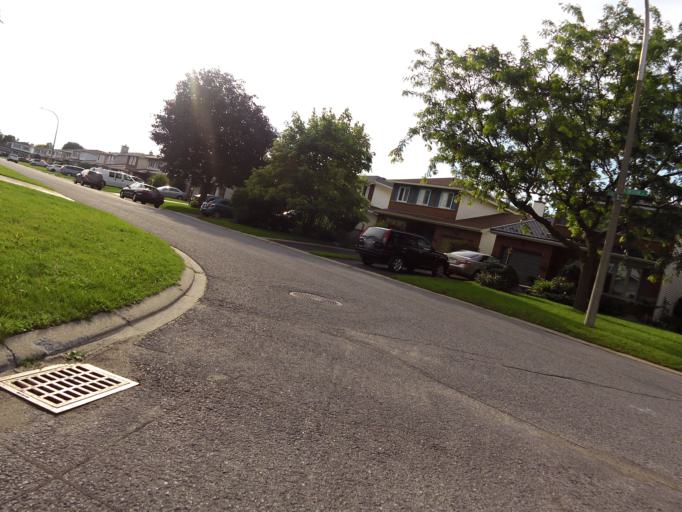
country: CA
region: Ontario
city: Ottawa
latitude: 45.3376
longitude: -75.7391
